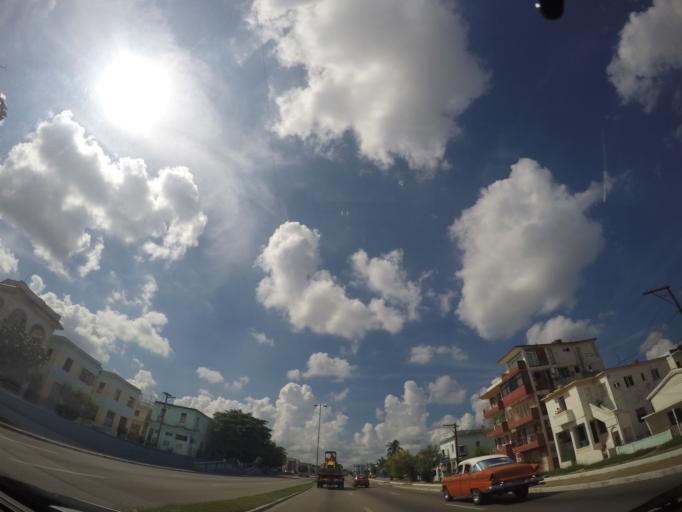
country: CU
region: La Habana
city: Cerro
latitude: 23.1087
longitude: -82.4186
